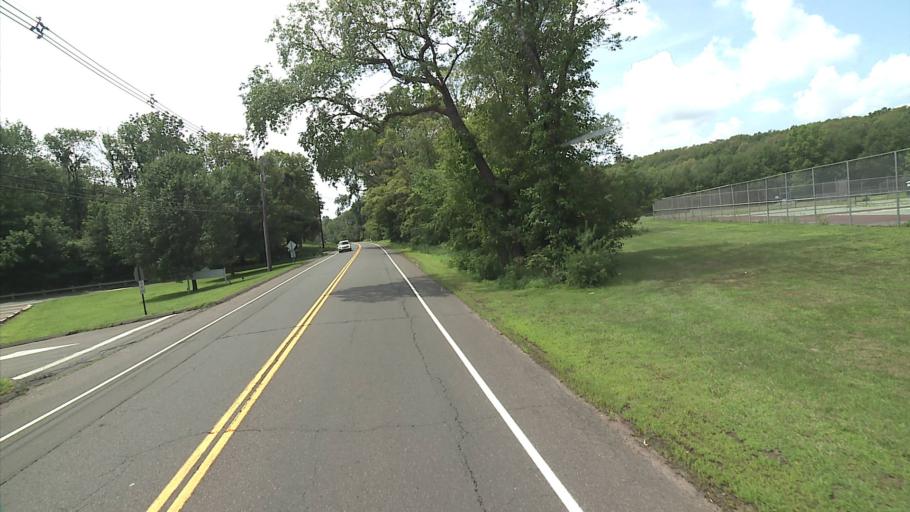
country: US
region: Connecticut
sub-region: New Haven County
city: Wallingford Center
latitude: 41.3899
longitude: -72.7944
